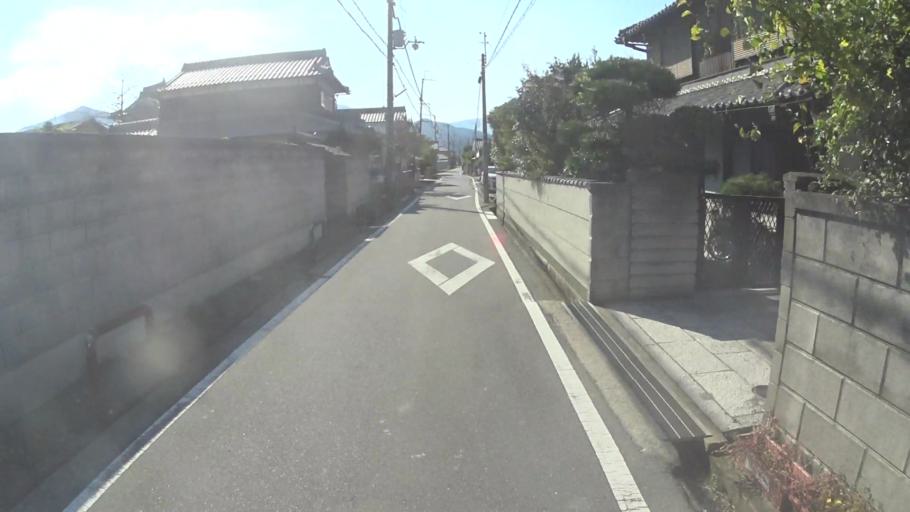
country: JP
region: Kyoto
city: Kameoka
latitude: 35.0171
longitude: 135.5468
